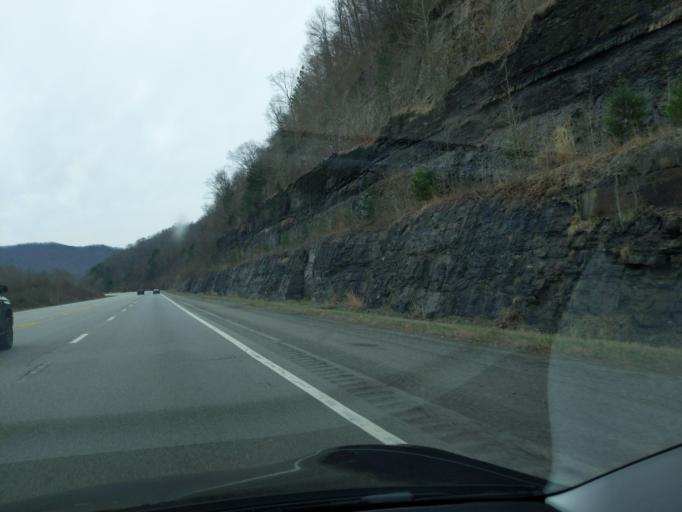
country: US
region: Kentucky
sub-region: Bell County
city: Pineville
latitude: 36.7725
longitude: -83.7305
